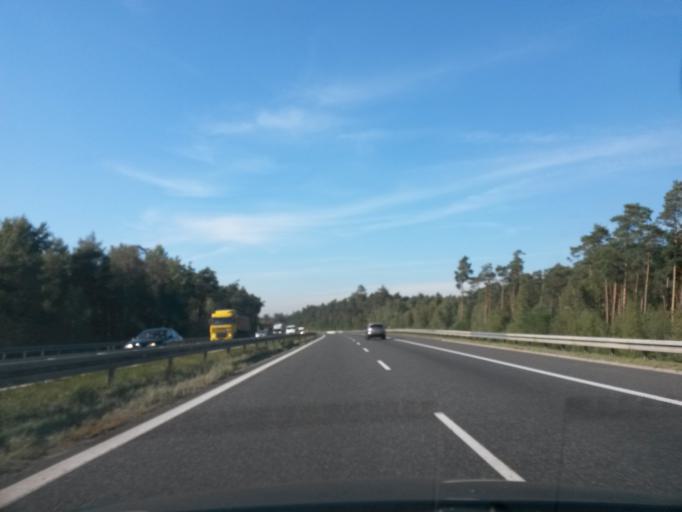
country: PL
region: Silesian Voivodeship
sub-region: Powiat gliwicki
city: Sosnicowice
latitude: 50.3592
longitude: 18.5179
